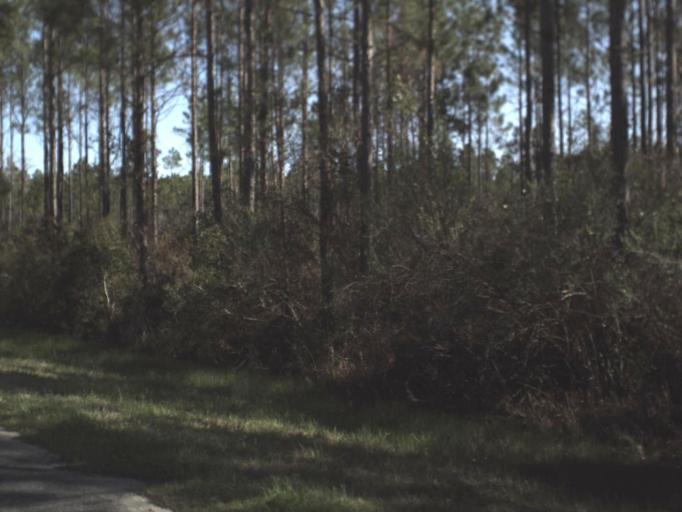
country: US
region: Florida
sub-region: Leon County
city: Woodville
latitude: 30.2805
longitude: -84.0424
